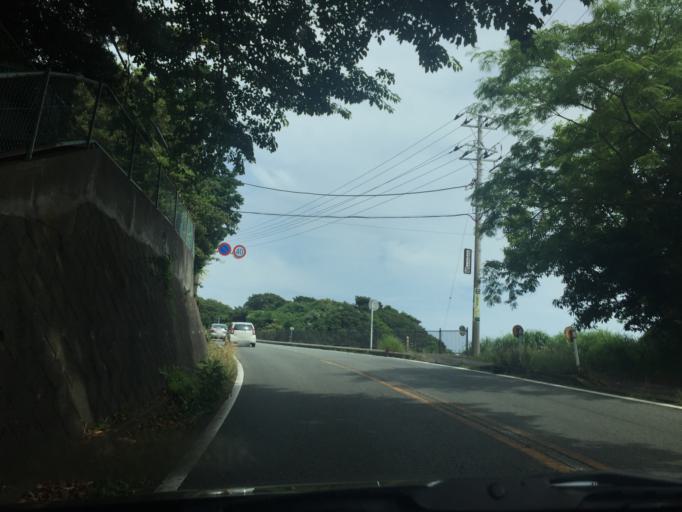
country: JP
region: Shizuoka
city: Shimoda
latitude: 34.7551
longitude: 139.0176
